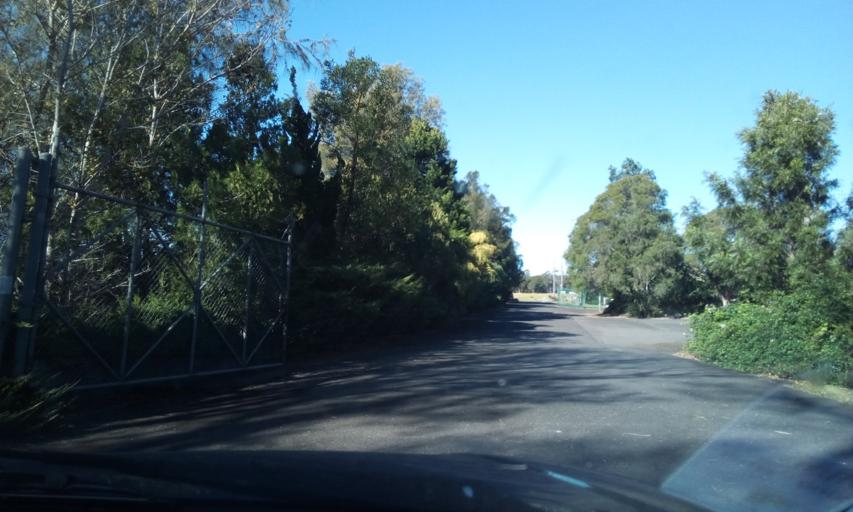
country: AU
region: New South Wales
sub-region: Wollongong
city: Dapto
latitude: -34.5265
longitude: 150.7746
